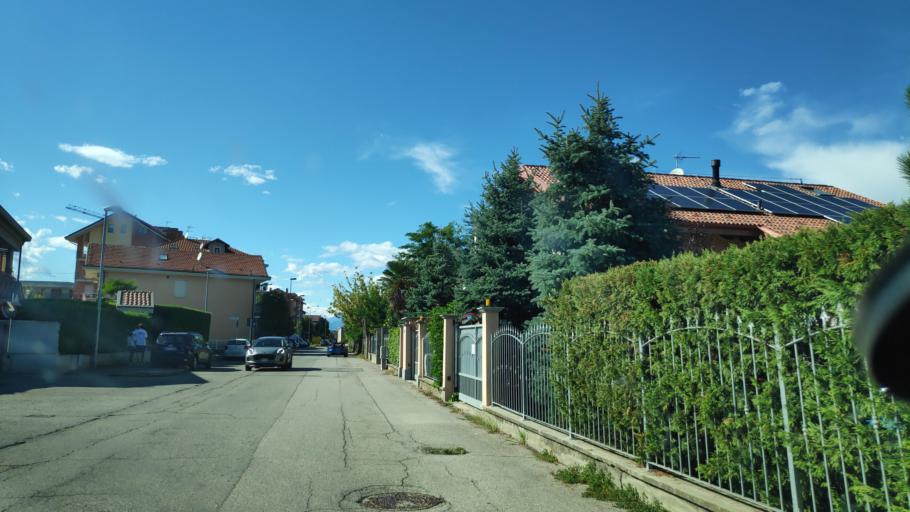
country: IT
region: Piedmont
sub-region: Provincia di Torino
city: La Loggia
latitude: 44.9531
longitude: 7.6758
